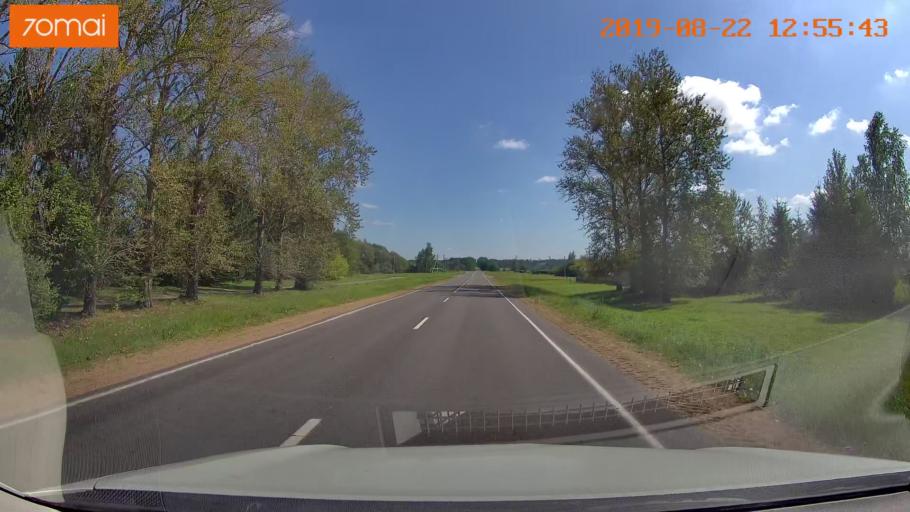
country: BY
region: Minsk
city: Prawdzinski
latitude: 53.4358
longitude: 27.7181
